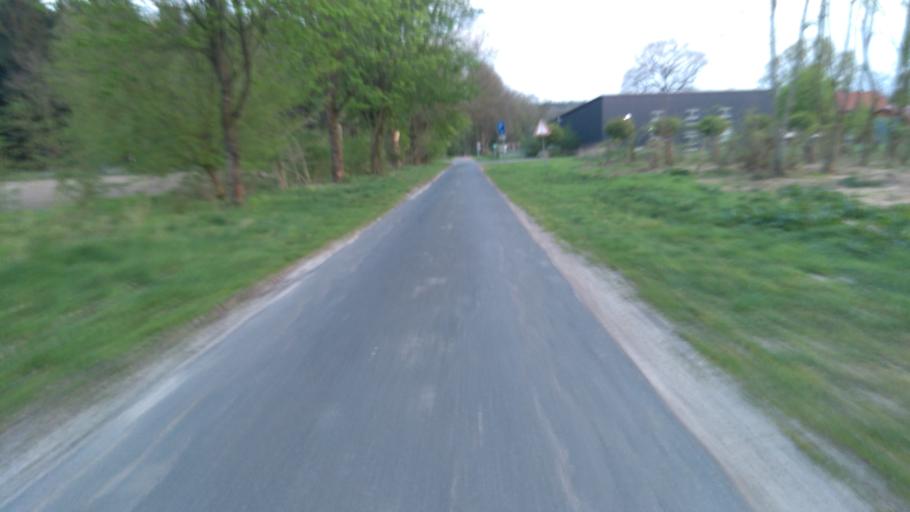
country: DE
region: Lower Saxony
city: Bargstedt
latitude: 53.4600
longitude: 9.4690
